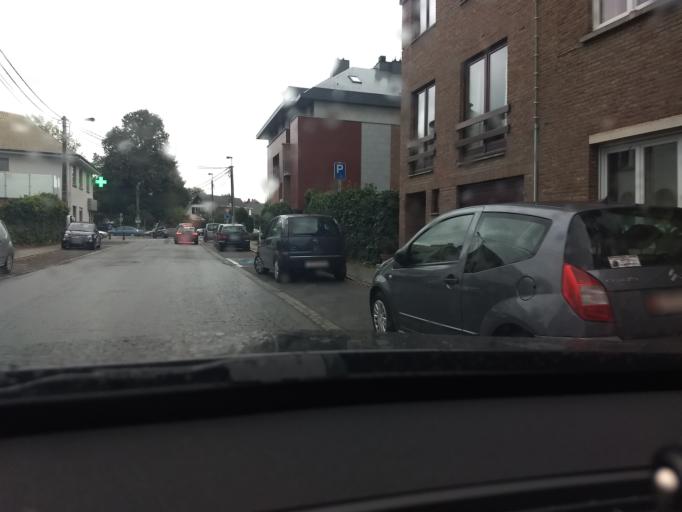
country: BE
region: Wallonia
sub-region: Province du Brabant Wallon
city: Braine-l'Alleud
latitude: 50.6784
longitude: 4.3788
